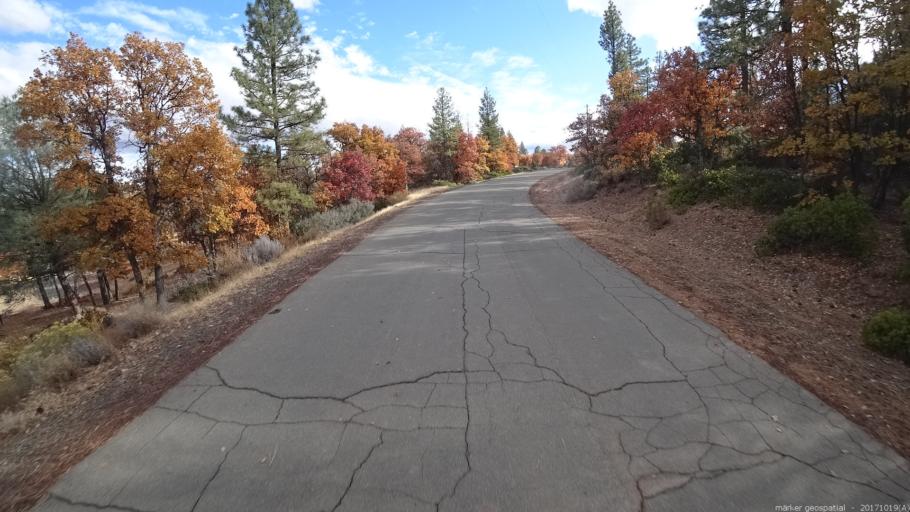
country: US
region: California
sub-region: Shasta County
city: Burney
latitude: 40.9710
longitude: -121.4409
